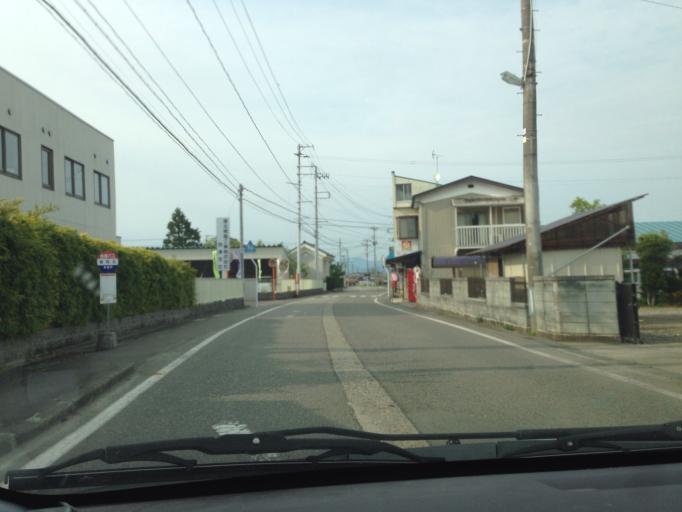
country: JP
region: Fukushima
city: Kitakata
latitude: 37.4591
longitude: 139.8940
